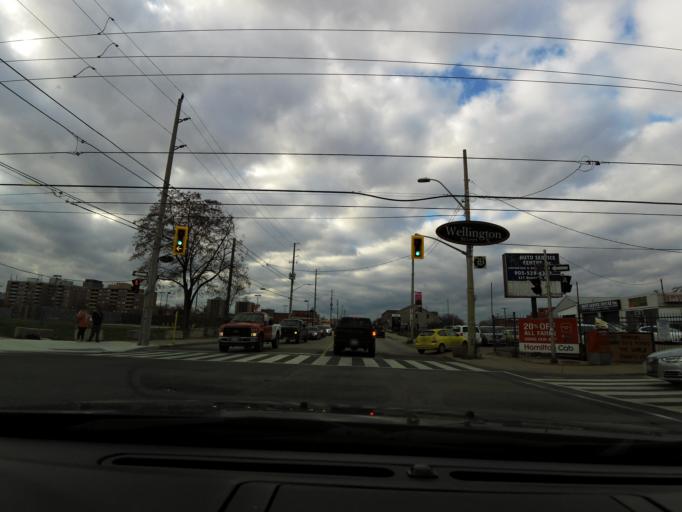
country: CA
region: Ontario
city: Hamilton
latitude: 43.2617
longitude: -79.8559
